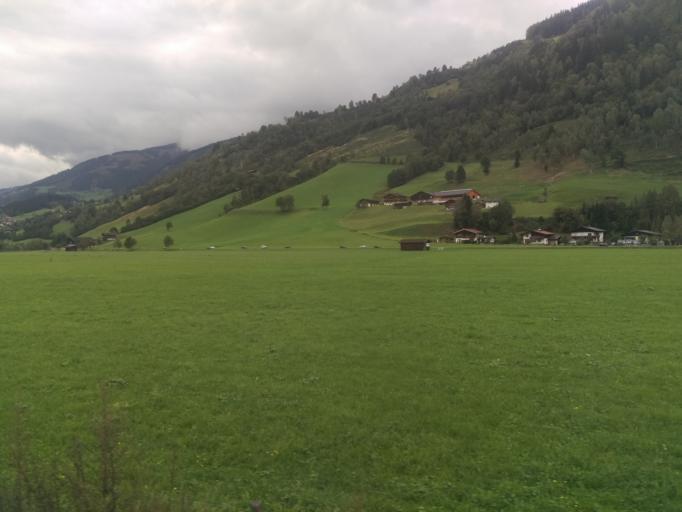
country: AT
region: Salzburg
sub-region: Politischer Bezirk Zell am See
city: Niedernsill
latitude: 47.2829
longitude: 12.6693
